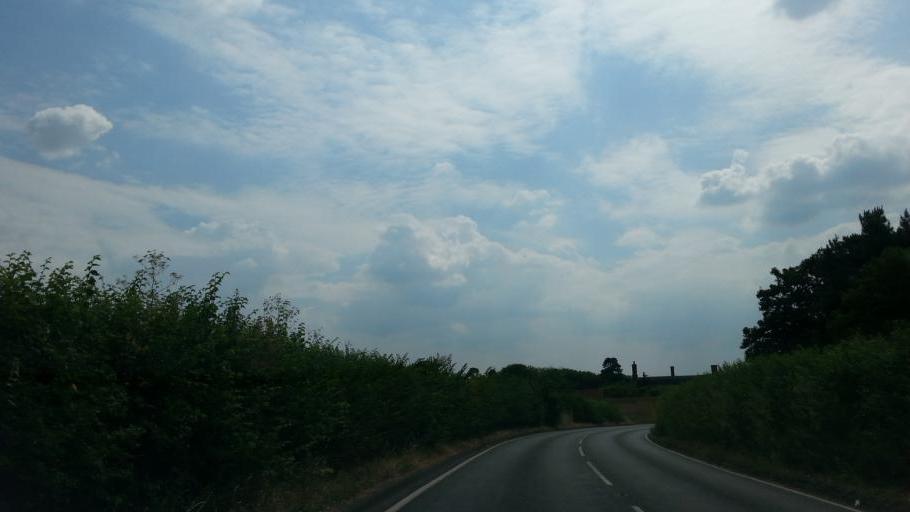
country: GB
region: England
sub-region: Suffolk
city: Lakenheath
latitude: 52.3830
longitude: 0.5271
